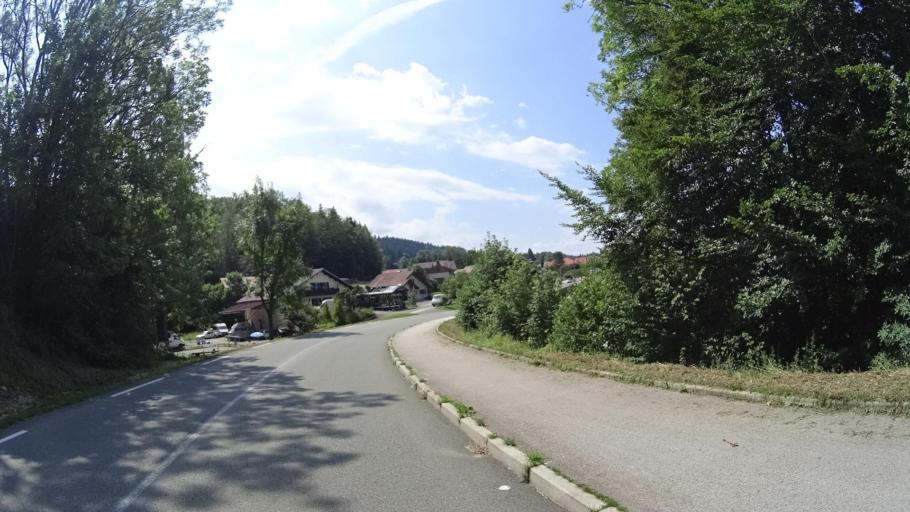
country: FR
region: Franche-Comte
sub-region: Departement du Doubs
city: Les Fourgs
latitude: 46.8205
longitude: 6.3301
